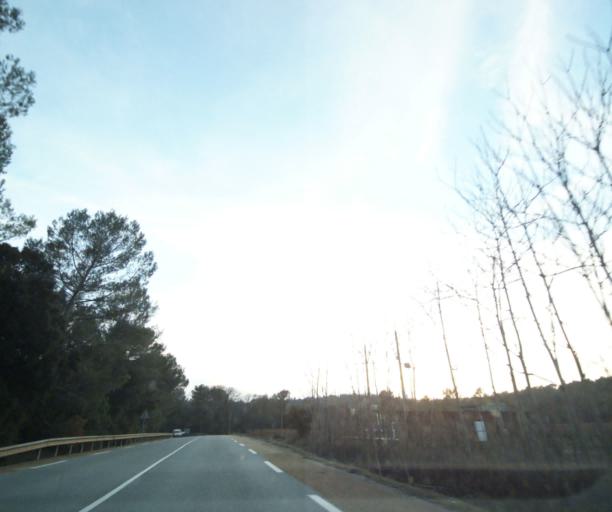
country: FR
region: Provence-Alpes-Cote d'Azur
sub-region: Departement du Var
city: La Motte
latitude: 43.4862
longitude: 6.5116
